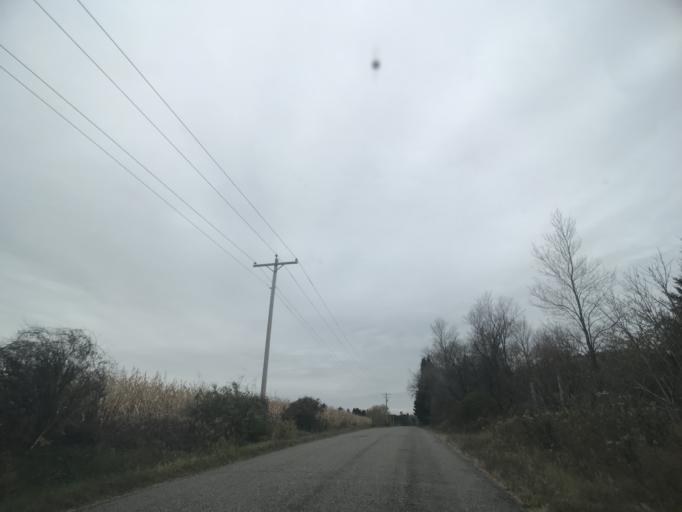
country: US
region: Wisconsin
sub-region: Menominee County
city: Legend Lake
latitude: 45.1812
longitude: -88.4624
